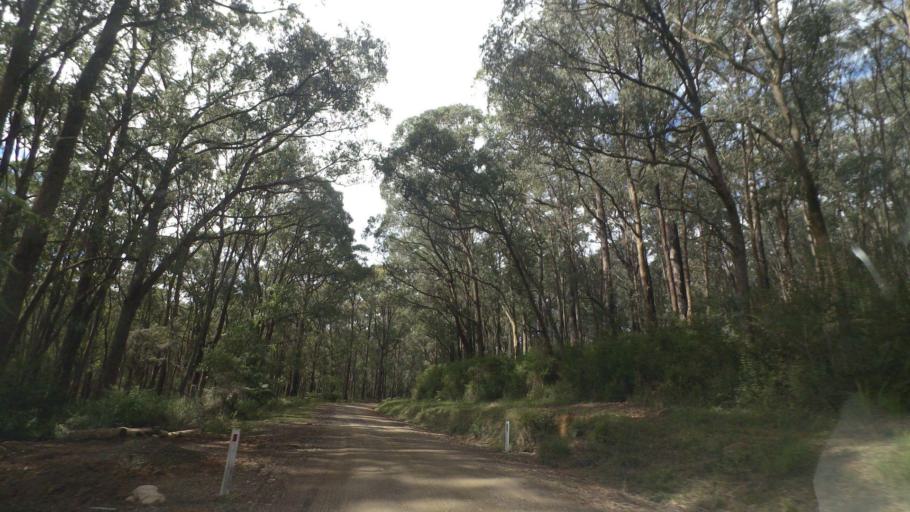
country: AU
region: Victoria
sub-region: Cardinia
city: Gembrook
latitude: -37.9098
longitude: 145.6192
